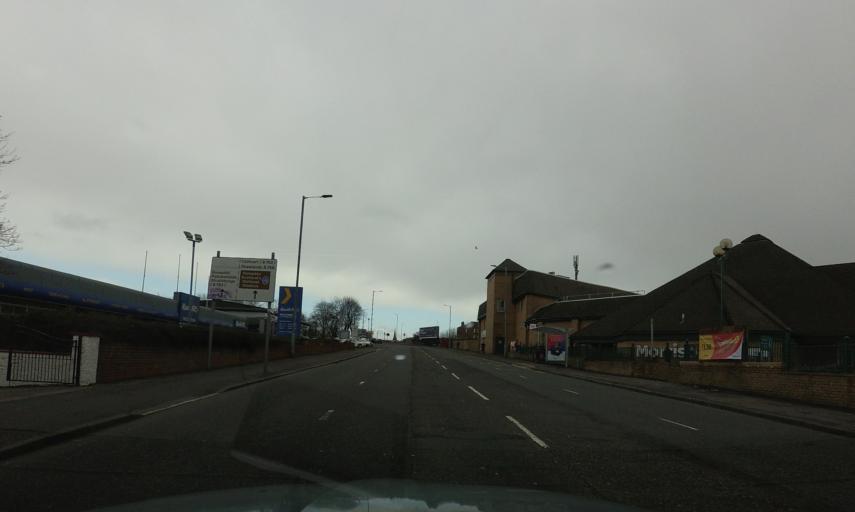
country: GB
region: Scotland
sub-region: East Renfrewshire
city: Giffnock
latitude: 55.8342
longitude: -4.2866
